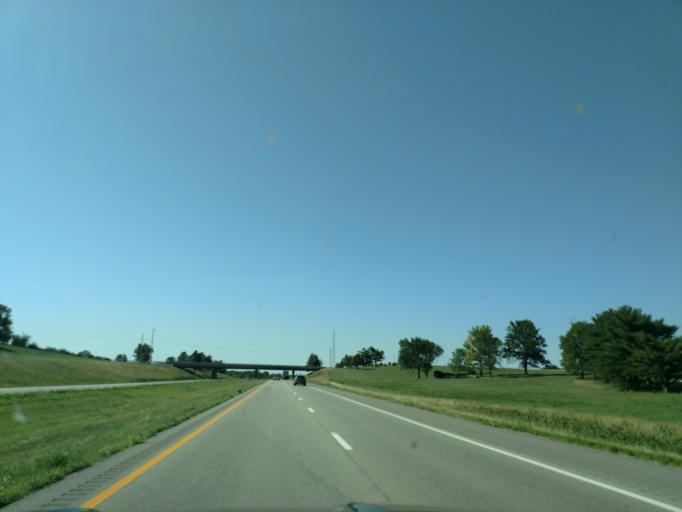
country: US
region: Missouri
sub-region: Andrew County
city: Country Club Village
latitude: 39.8124
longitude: -94.8027
